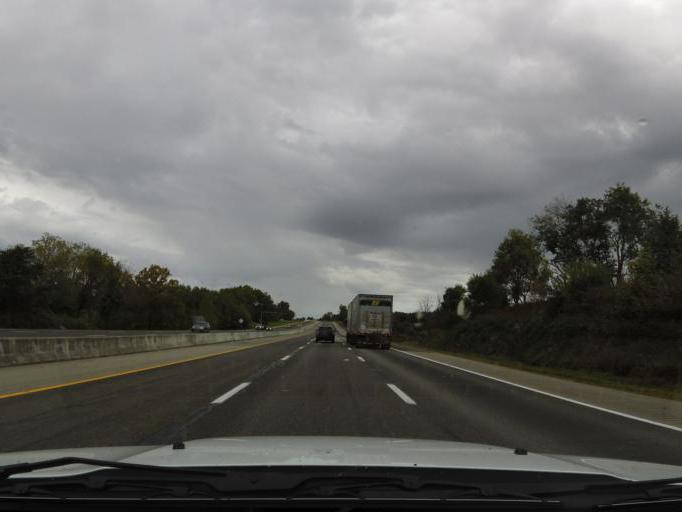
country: US
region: Kentucky
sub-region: Laurel County
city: London
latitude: 37.0539
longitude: -84.0983
